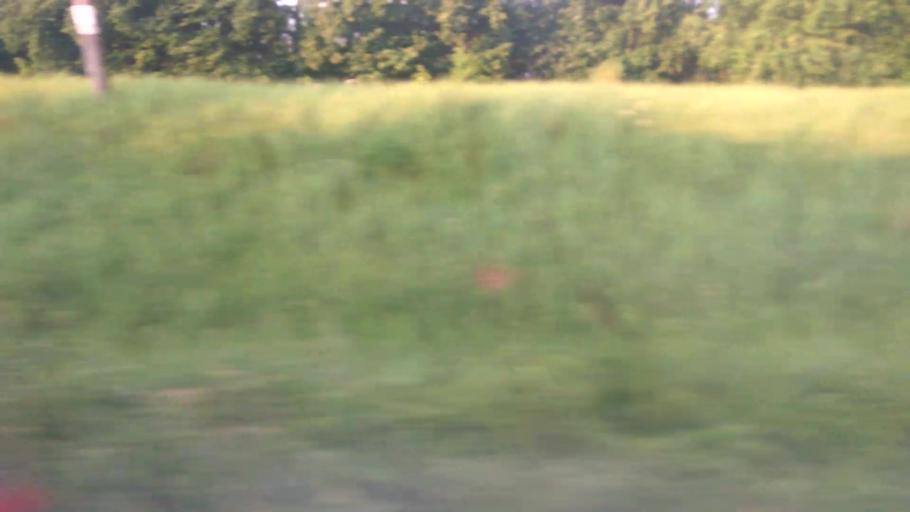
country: RU
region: Moskovskaya
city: Stupino
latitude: 54.8909
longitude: 38.0954
